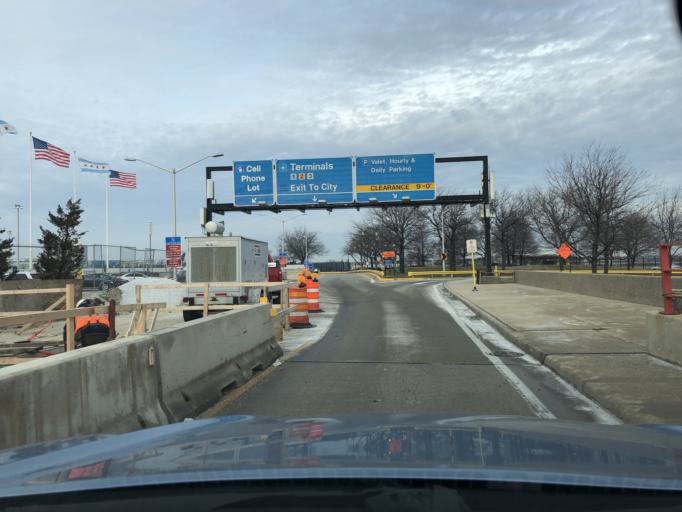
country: US
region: Illinois
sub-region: Cook County
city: Rosemont
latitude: 41.9812
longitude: -87.9010
